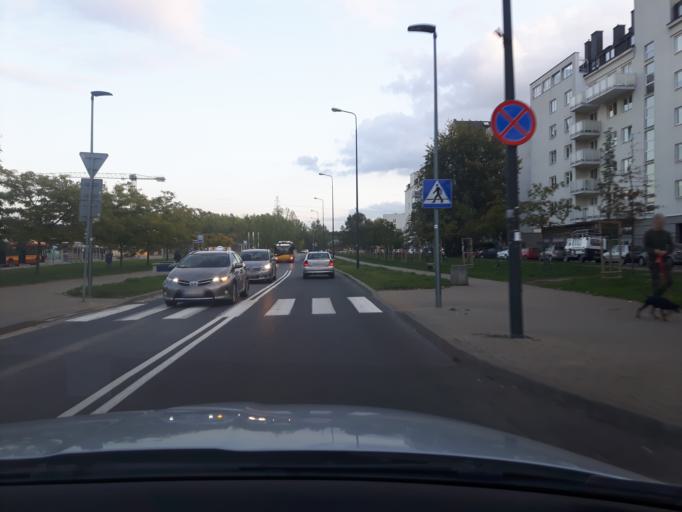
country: PL
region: Masovian Voivodeship
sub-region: Warszawa
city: Kabaty
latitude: 52.1297
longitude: 21.0673
